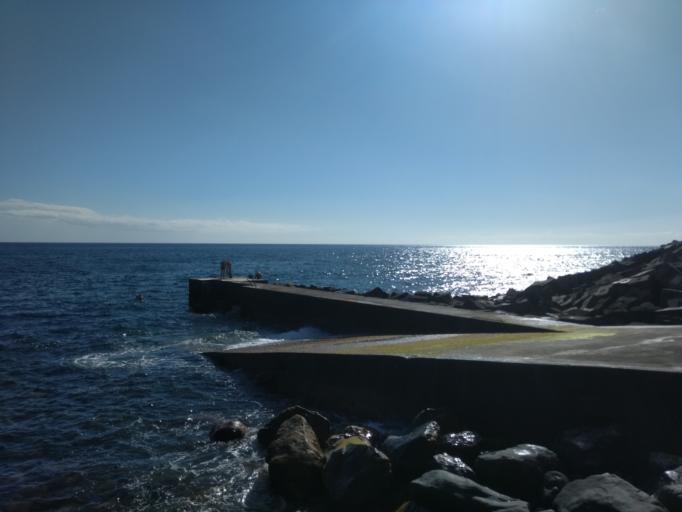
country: PT
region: Madeira
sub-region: Calheta
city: Estreito da Calheta
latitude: 32.7351
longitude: -17.2084
